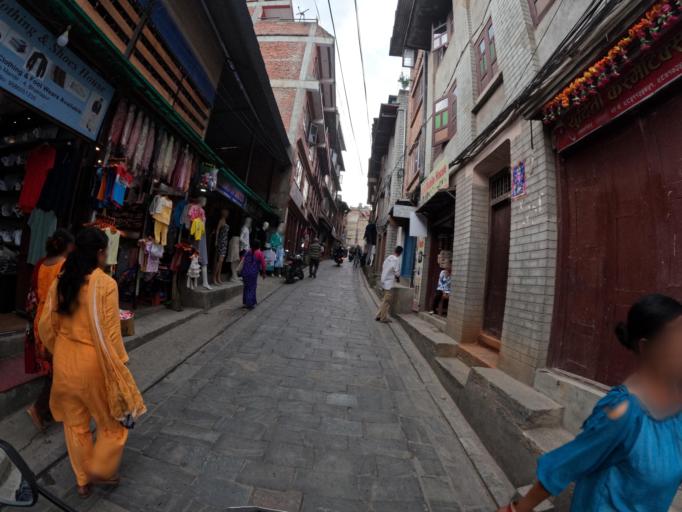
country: NP
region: Central Region
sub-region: Bagmati Zone
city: Bhaktapur
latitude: 27.6693
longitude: 85.4281
